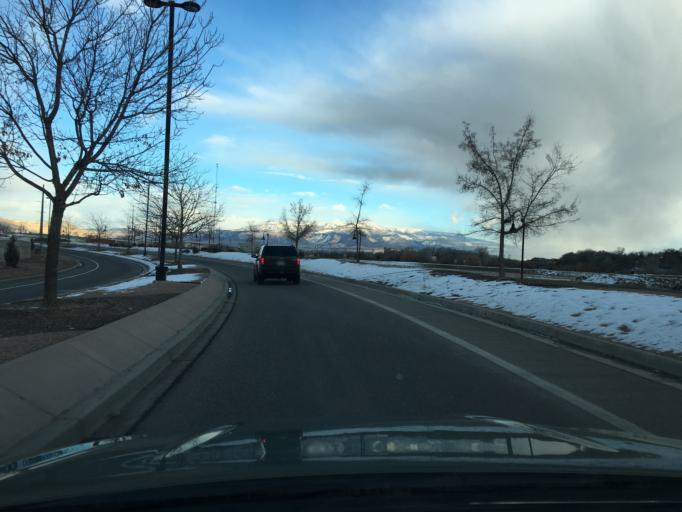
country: US
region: Colorado
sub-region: Mesa County
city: Grand Junction
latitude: 39.0561
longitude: -108.5487
